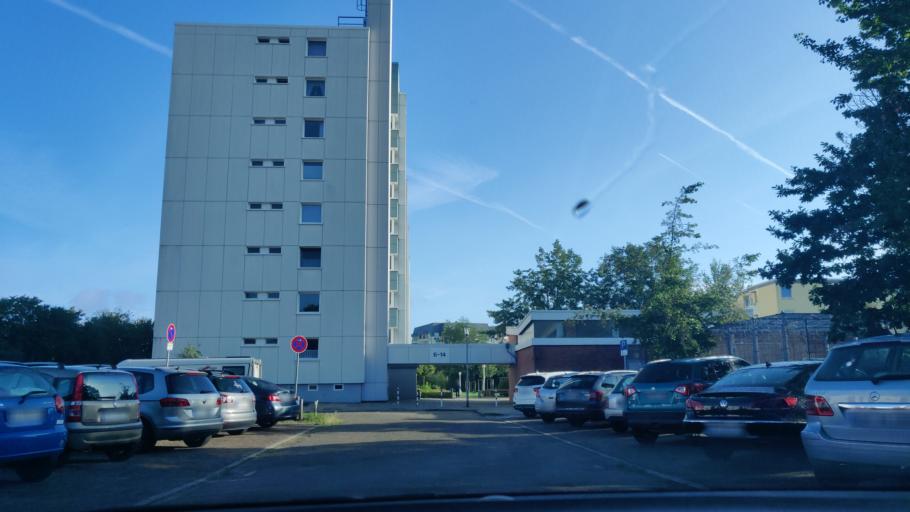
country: DE
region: Lower Saxony
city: Cuxhaven
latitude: 53.8873
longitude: 8.6733
